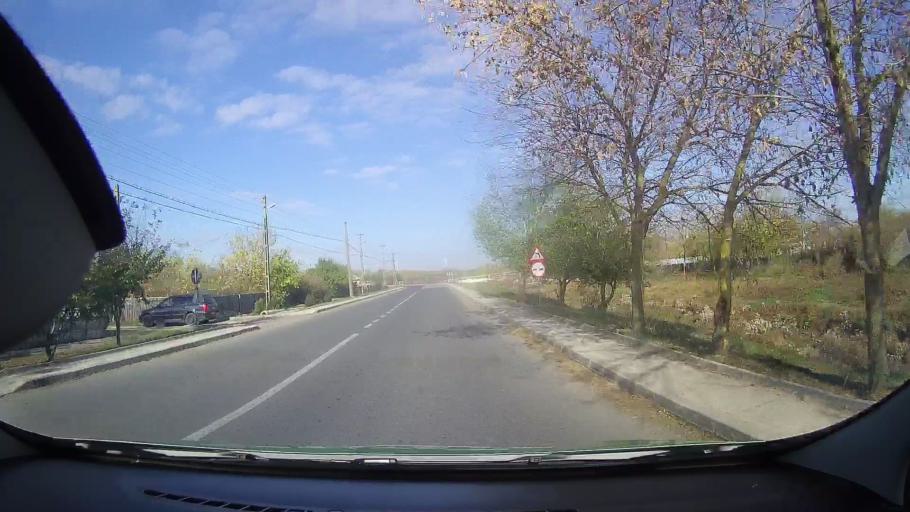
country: RO
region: Tulcea
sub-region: Comuna Valea Nucarilor
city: Valea Nucarilor
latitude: 45.0417
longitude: 28.9358
